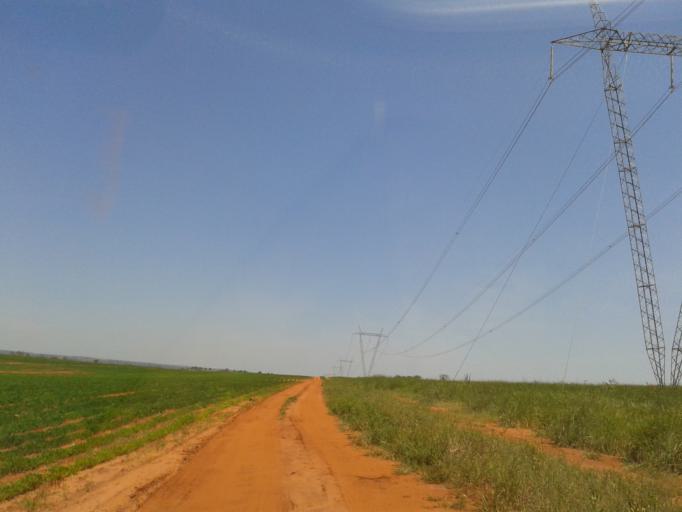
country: BR
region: Minas Gerais
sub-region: Santa Vitoria
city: Santa Vitoria
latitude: -19.0747
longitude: -50.4605
